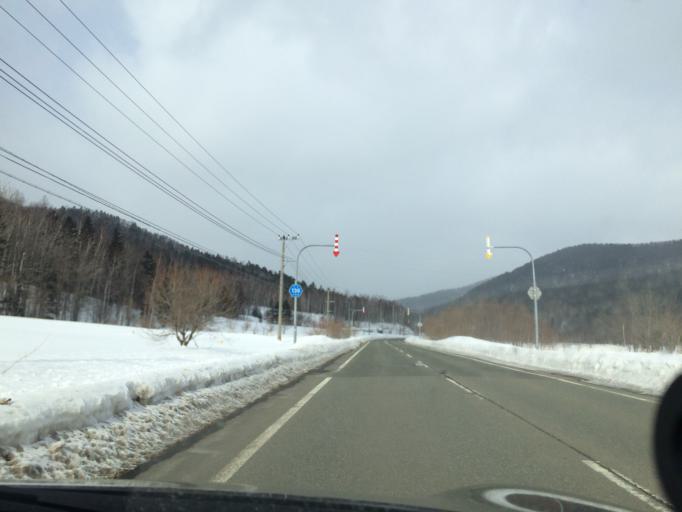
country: JP
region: Hokkaido
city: Shimo-furano
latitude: 43.0472
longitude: 142.5325
